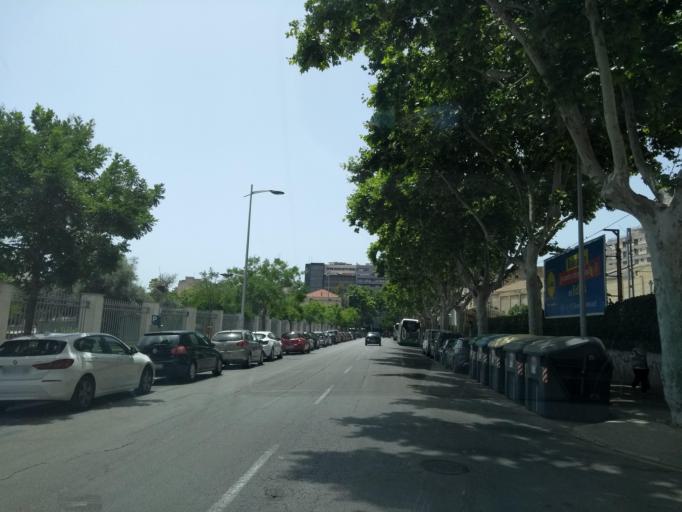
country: ES
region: Balearic Islands
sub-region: Illes Balears
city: Palma
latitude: 39.5776
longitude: 2.6554
